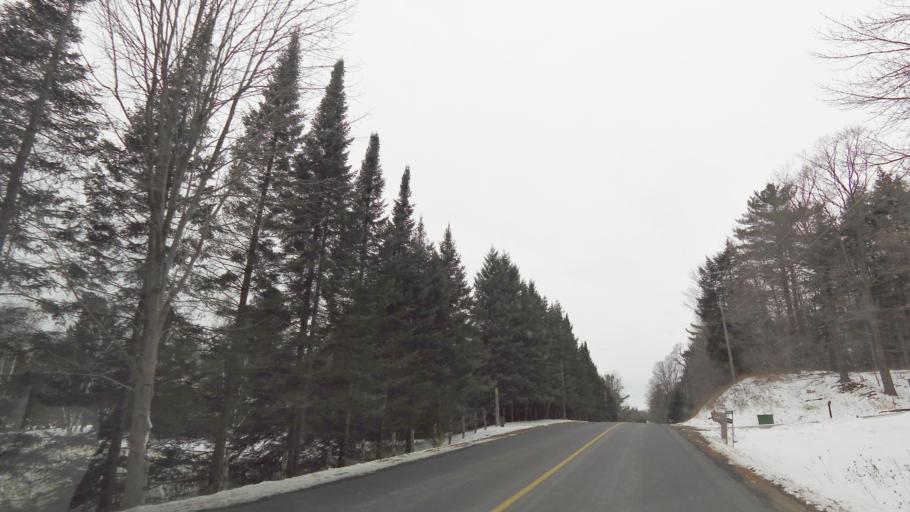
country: CA
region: Ontario
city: Bradford West Gwillimbury
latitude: 43.9460
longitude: -79.6375
